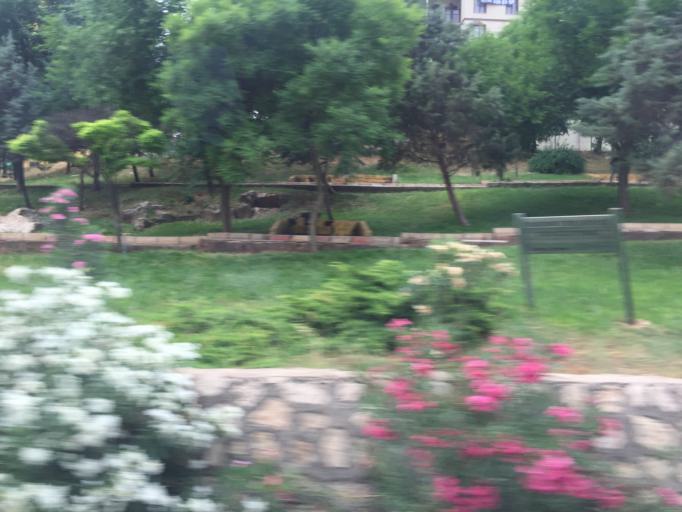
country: TR
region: Gaziantep
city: Gaziantep
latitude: 37.0531
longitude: 37.4200
